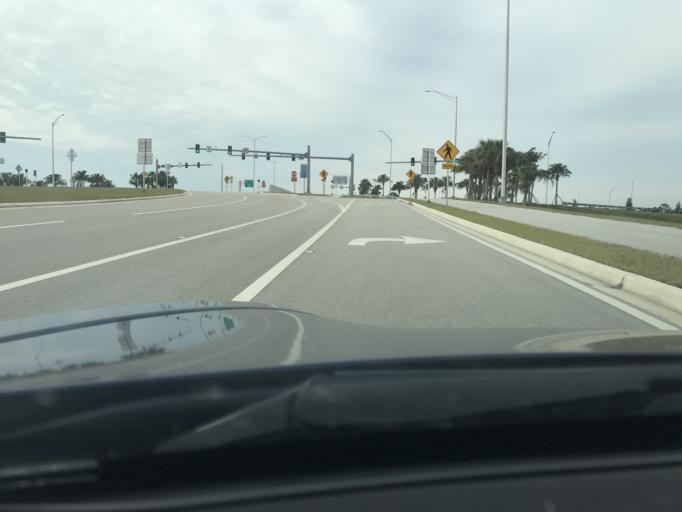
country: US
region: Florida
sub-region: Brevard County
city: Grant-Valkaria
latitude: 27.8961
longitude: -80.5929
